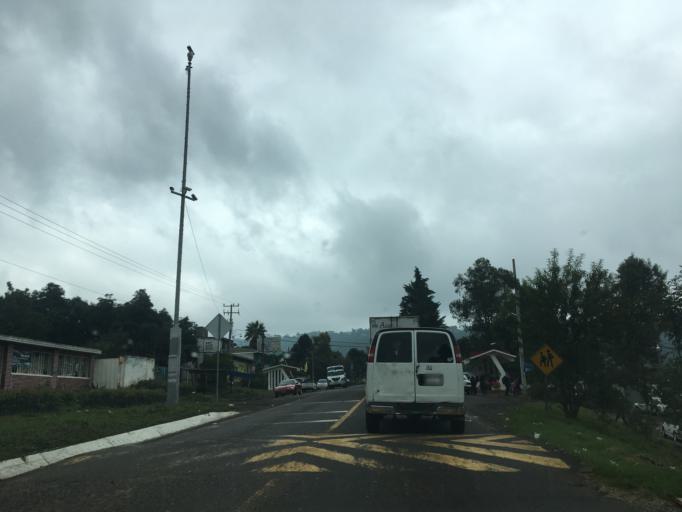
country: MX
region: Michoacan
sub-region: Uruapan
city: Toreo Bajo (El Toreo Bajo)
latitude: 19.4554
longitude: -102.0005
